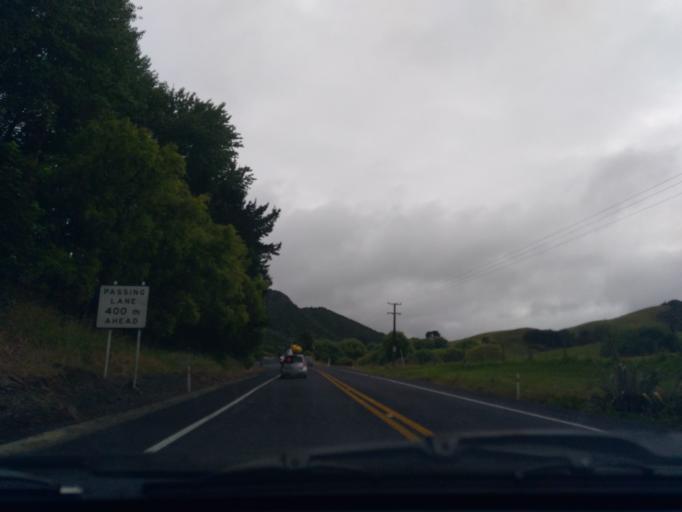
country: NZ
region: Auckland
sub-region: Auckland
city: Wellsford
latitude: -36.1240
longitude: 174.4336
